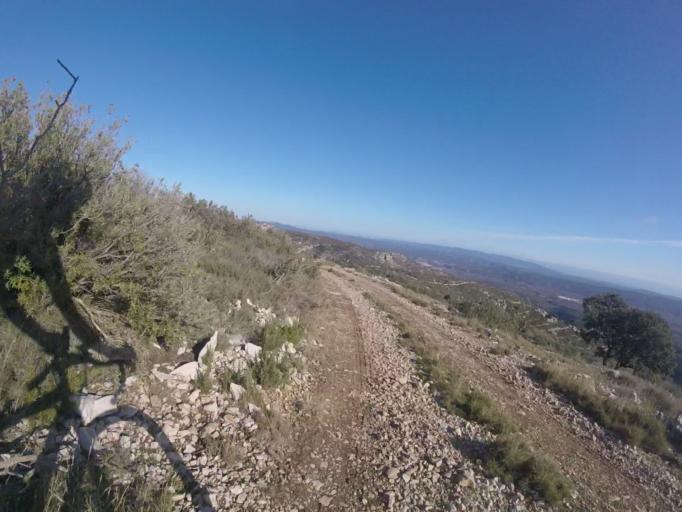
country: ES
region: Valencia
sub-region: Provincia de Castello
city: Sarratella
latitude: 40.3000
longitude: 0.0384
